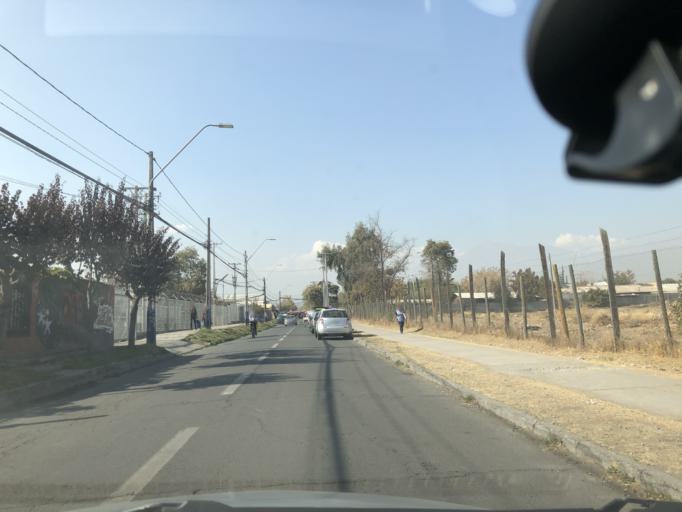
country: CL
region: Santiago Metropolitan
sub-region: Provincia de Cordillera
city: Puente Alto
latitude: -33.5889
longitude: -70.5732
